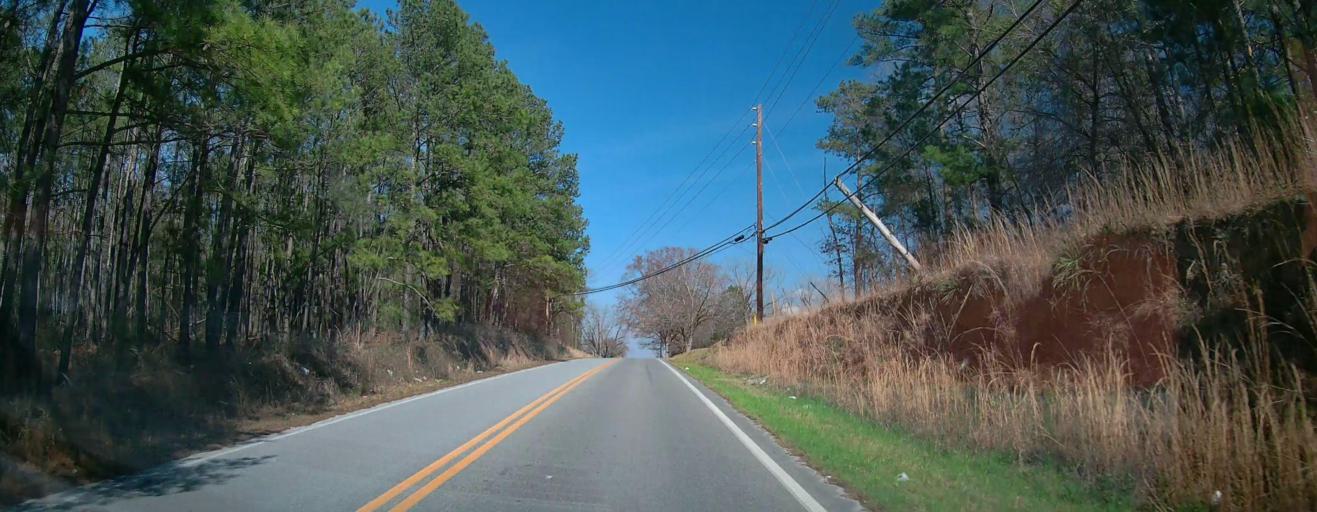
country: US
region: Georgia
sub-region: Wilkinson County
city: Gordon
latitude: 32.8897
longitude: -83.3153
